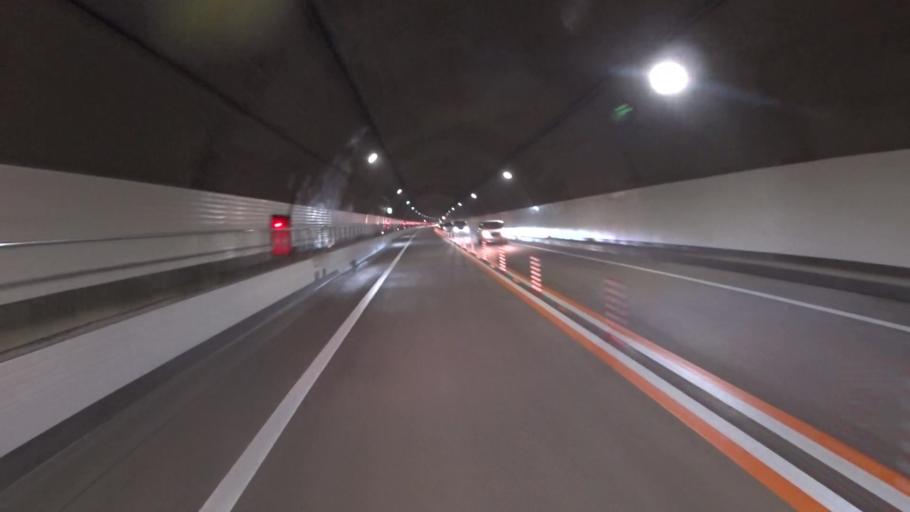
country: JP
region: Kyoto
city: Ayabe
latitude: 35.2430
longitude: 135.3429
